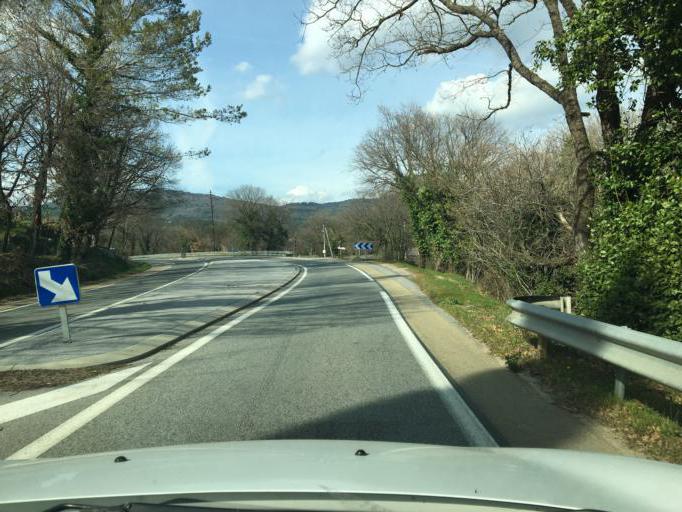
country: FR
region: Provence-Alpes-Cote d'Azur
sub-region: Departement du Var
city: Figanieres
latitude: 43.5607
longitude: 6.5126
